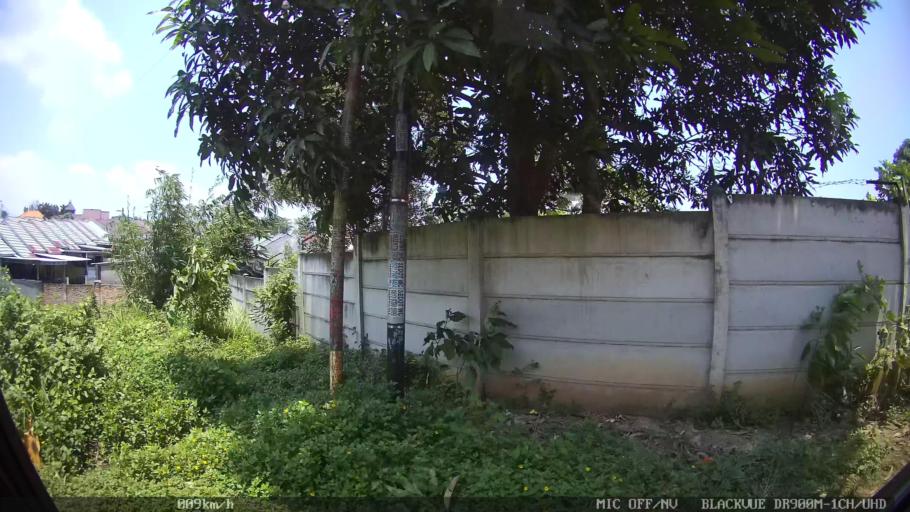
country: ID
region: Lampung
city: Kedaton
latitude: -5.3672
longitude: 105.2634
